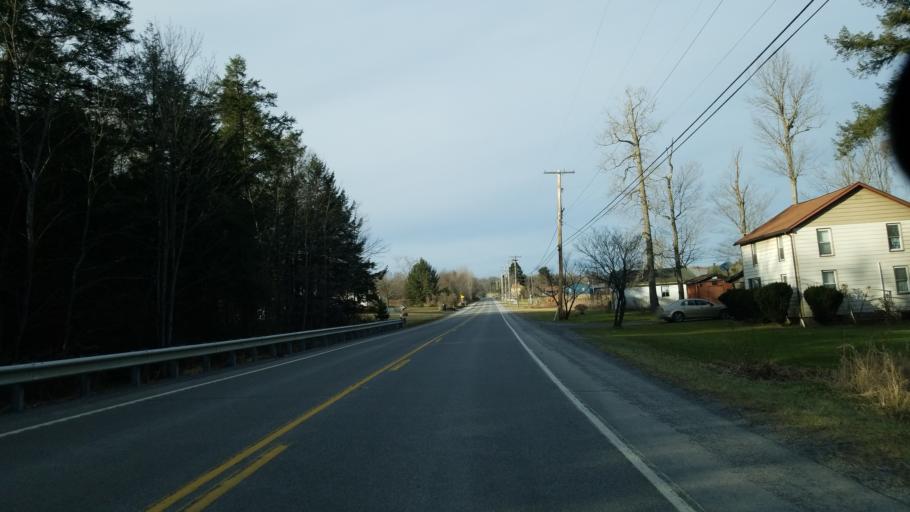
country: US
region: Pennsylvania
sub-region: Clearfield County
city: Curwensville
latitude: 41.0009
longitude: -78.6348
